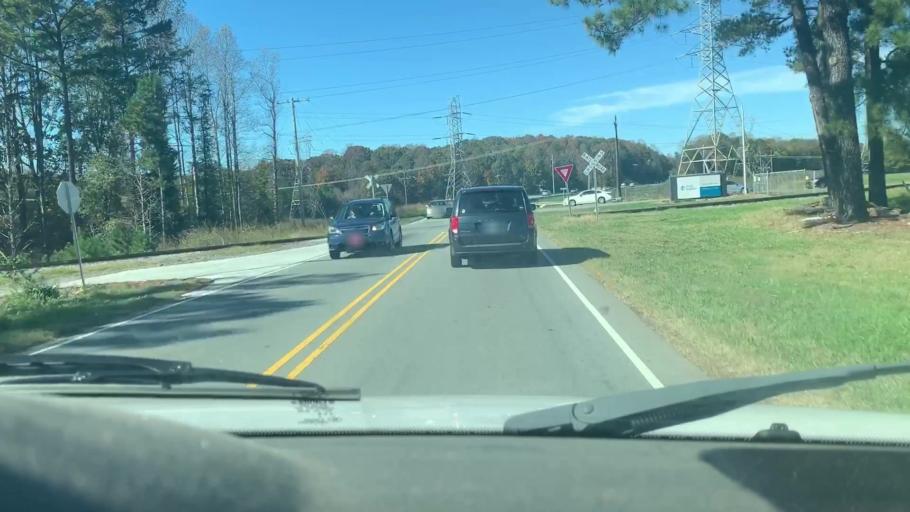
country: US
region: North Carolina
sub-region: Lincoln County
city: Lowesville
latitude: 35.4280
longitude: -80.9604
